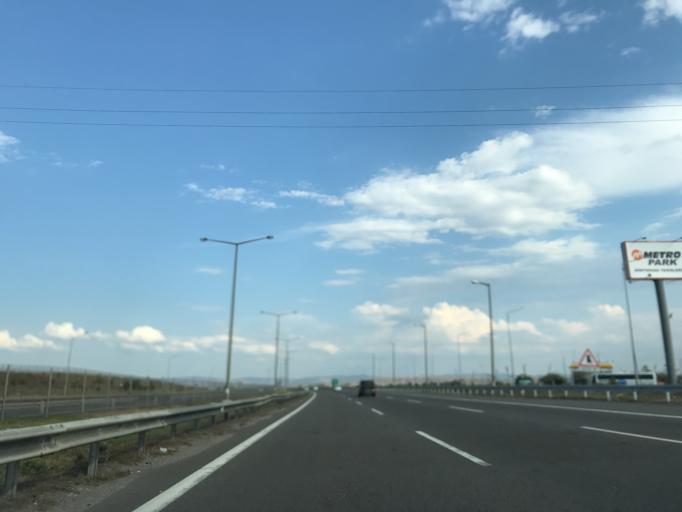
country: TR
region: Bolu
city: Dortdivan
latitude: 40.7493
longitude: 32.0847
